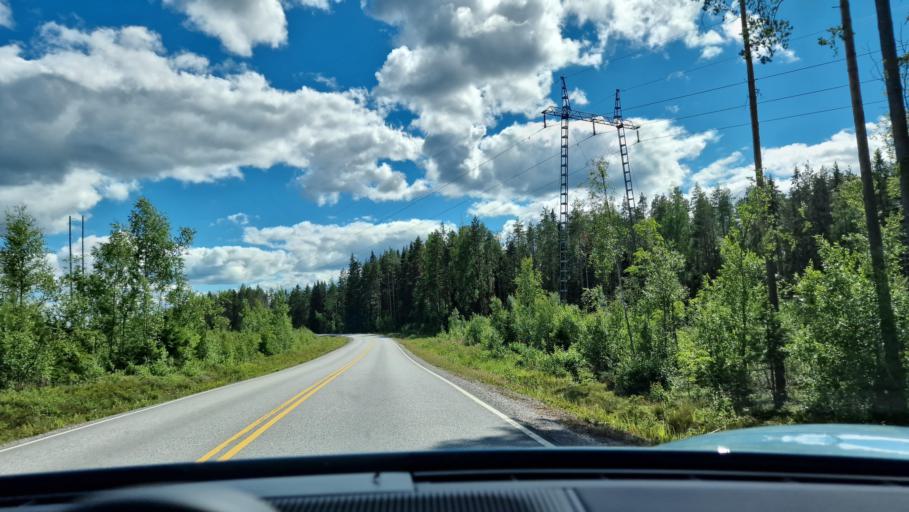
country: FI
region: Central Finland
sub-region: Saarijaervi-Viitasaari
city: Pylkoenmaeki
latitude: 62.6494
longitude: 24.5724
